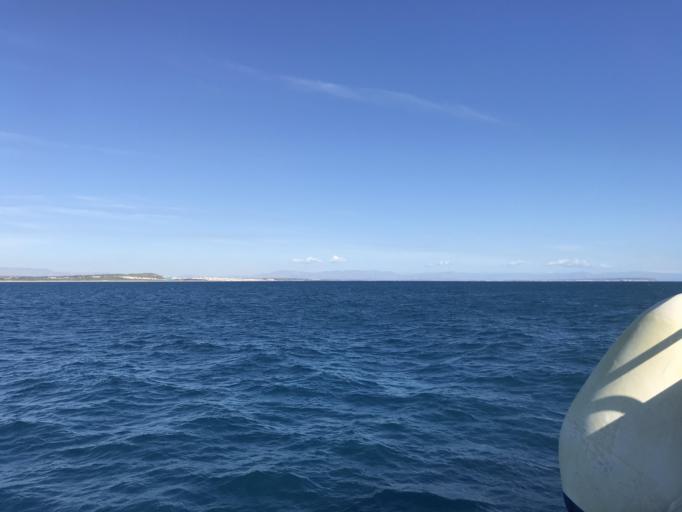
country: ES
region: Valencia
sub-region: Provincia de Alicante
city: Torrevieja
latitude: 38.0140
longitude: -0.6265
